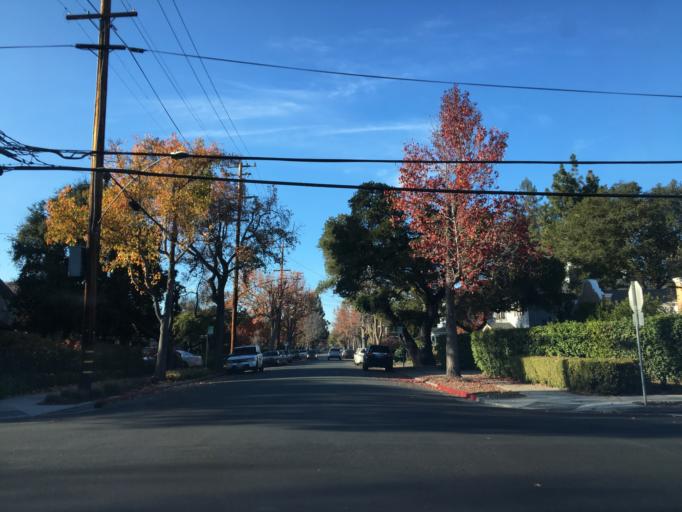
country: US
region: California
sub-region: Santa Clara County
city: Palo Alto
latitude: 37.4436
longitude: -122.1516
